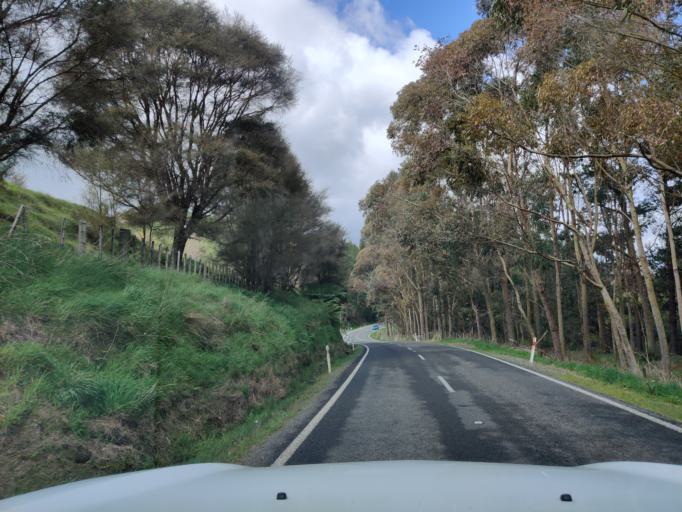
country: NZ
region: Manawatu-Wanganui
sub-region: Ruapehu District
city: Waiouru
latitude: -39.6569
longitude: 175.3296
